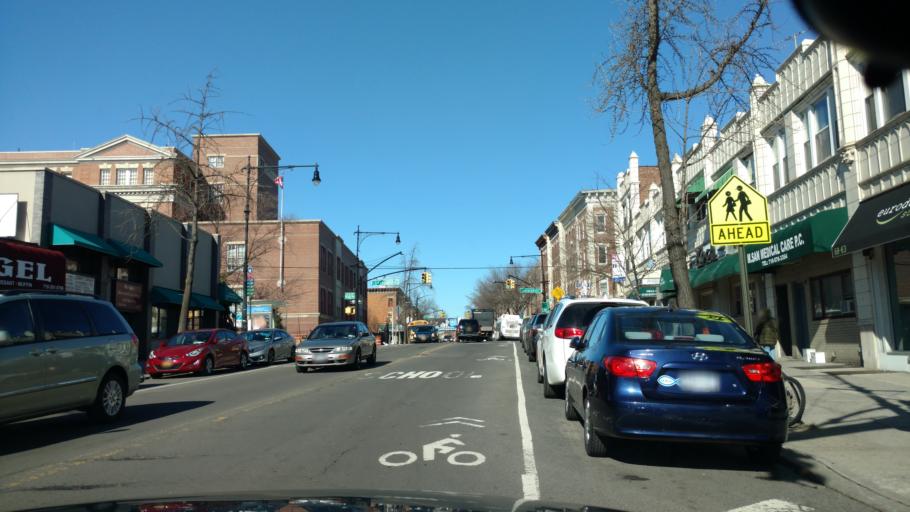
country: US
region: New York
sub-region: Kings County
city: East New York
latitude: 40.7035
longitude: -73.8955
